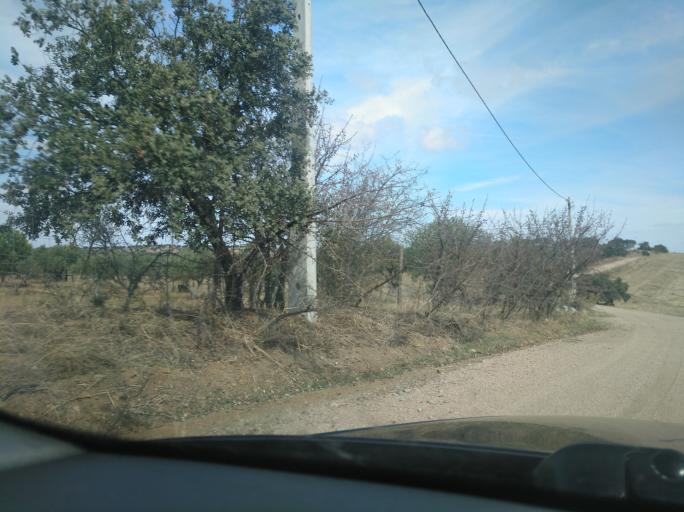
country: PT
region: Portalegre
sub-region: Campo Maior
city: Campo Maior
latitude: 39.0423
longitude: -7.0573
